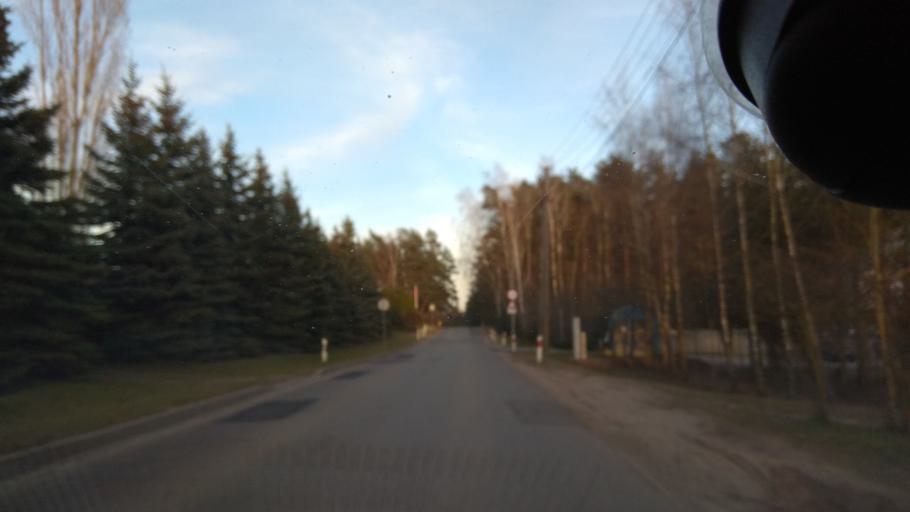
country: LT
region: Vilnius County
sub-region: Vilnius
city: Fabijoniskes
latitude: 54.7569
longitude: 25.2378
